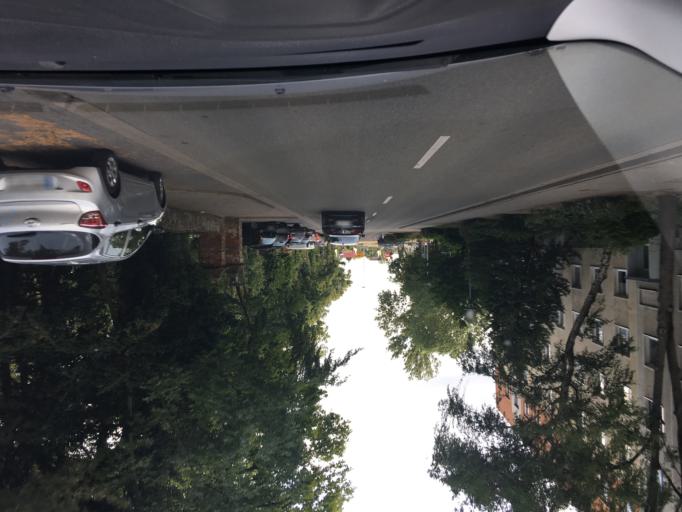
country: DE
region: Saxony-Anhalt
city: Wolmirstedt
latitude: 52.2508
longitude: 11.6282
